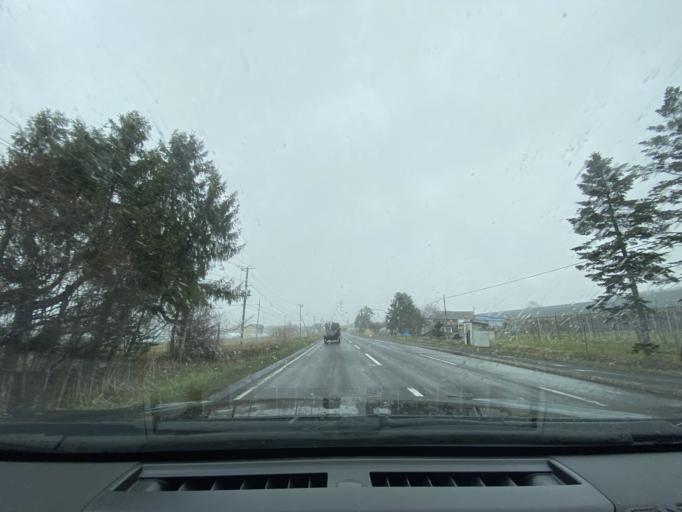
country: JP
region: Hokkaido
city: Fukagawa
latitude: 43.7122
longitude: 142.1543
